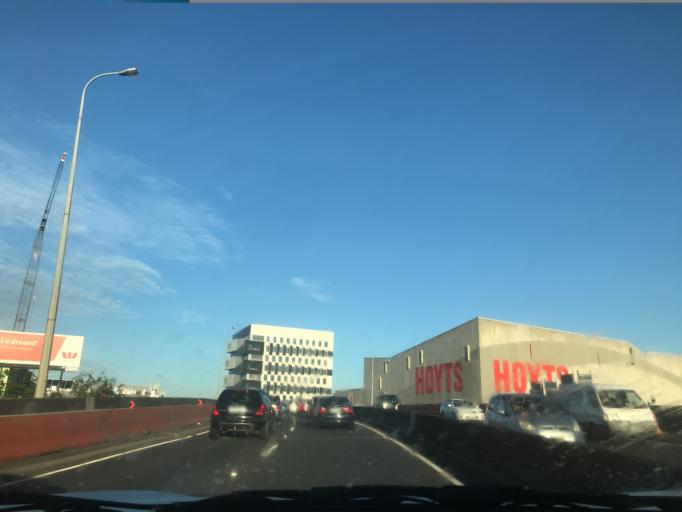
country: NZ
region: Auckland
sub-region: Auckland
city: Tamaki
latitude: -36.9153
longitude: 174.8435
